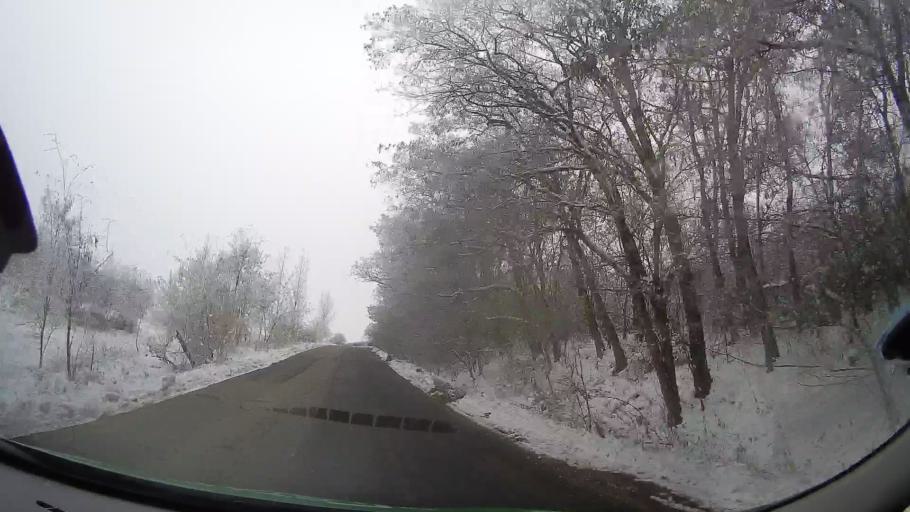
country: RO
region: Bacau
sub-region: Comuna Glavanesti
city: Frumuselu
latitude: 46.2630
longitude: 27.3263
